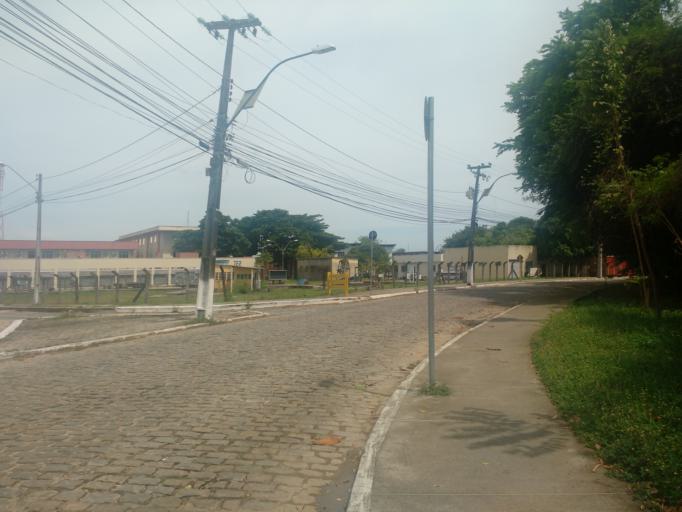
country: BR
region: Ceara
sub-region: Fortaleza
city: Fortaleza
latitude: -3.7459
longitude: -38.5779
